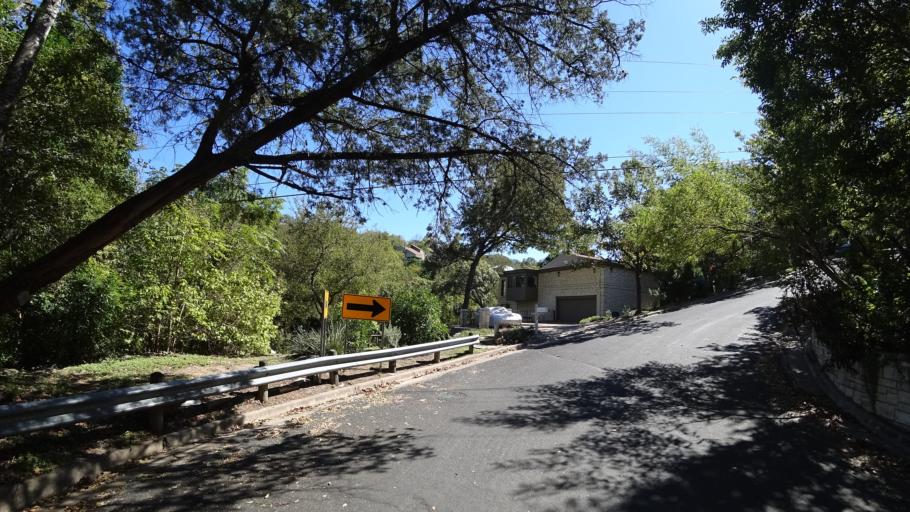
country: US
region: Texas
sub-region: Travis County
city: West Lake Hills
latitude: 30.3366
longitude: -97.7649
